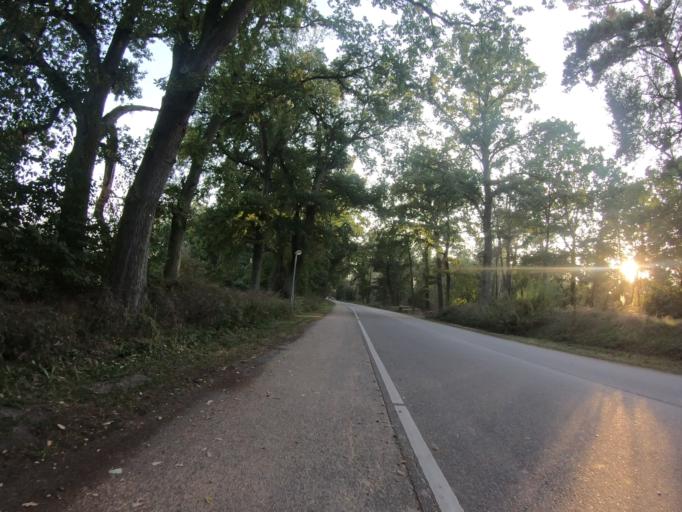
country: DE
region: Lower Saxony
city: Calberlah
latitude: 52.4485
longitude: 10.6119
